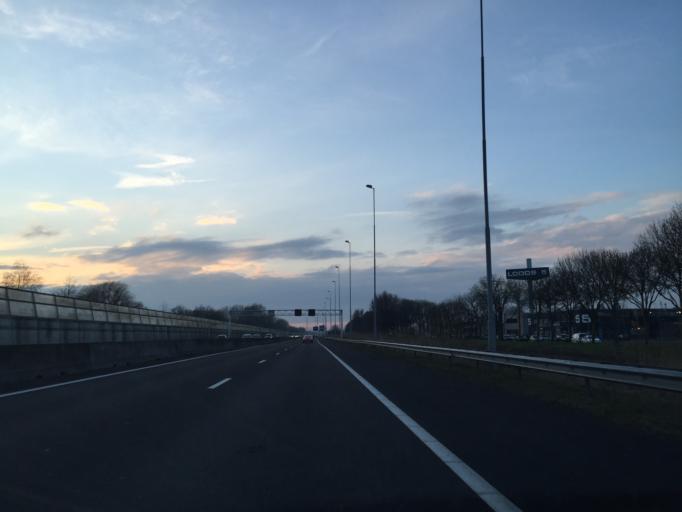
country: NL
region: South Holland
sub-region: Gemeente Sliedrecht
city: Sliedrecht
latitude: 51.8290
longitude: 4.7652
